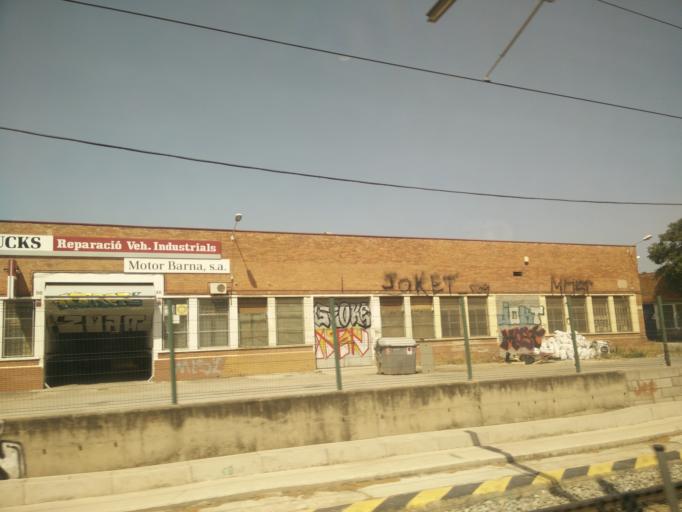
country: ES
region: Catalonia
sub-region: Provincia de Barcelona
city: Sant Marti
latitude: 41.4284
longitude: 2.2060
